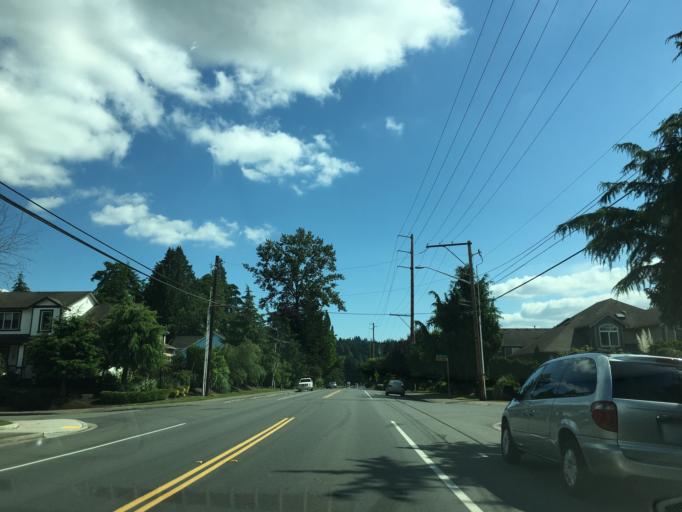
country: US
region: Washington
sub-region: King County
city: Kenmore
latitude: 47.7606
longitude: -122.2336
